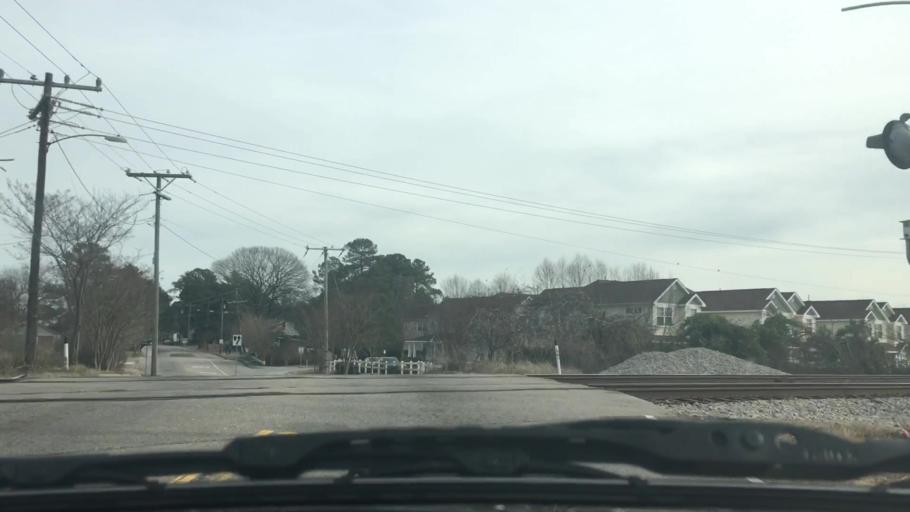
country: US
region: Virginia
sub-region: City of Norfolk
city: Norfolk
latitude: 36.8905
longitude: -76.2548
